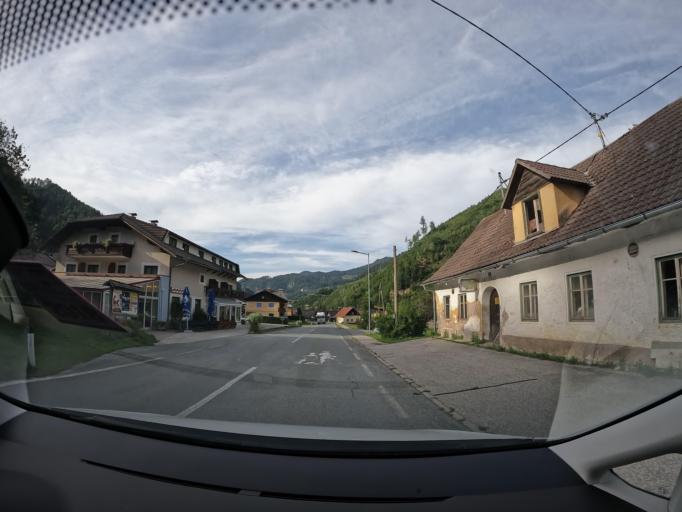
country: AT
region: Carinthia
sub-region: Politischer Bezirk Volkermarkt
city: Bad Eisenkappel
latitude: 46.4721
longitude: 14.5930
